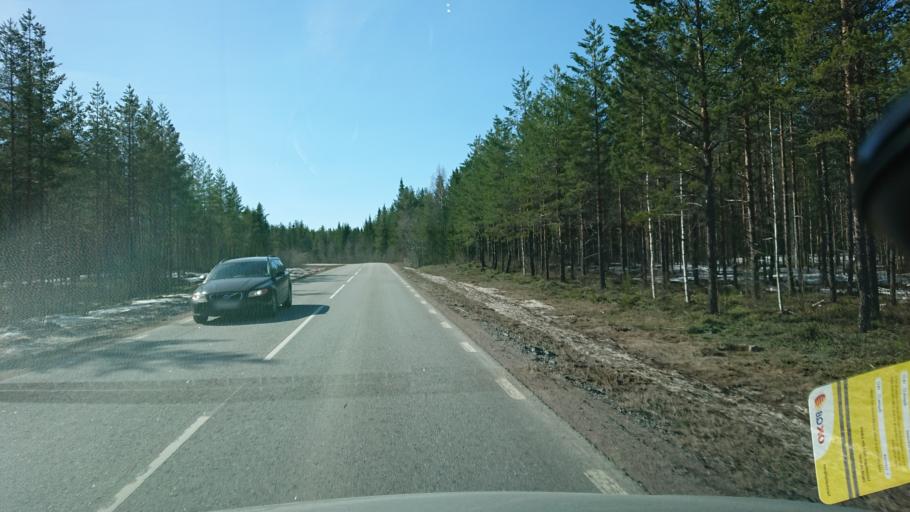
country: SE
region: Vaesternorrland
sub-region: Solleftea Kommun
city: As
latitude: 63.6306
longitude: 16.4421
